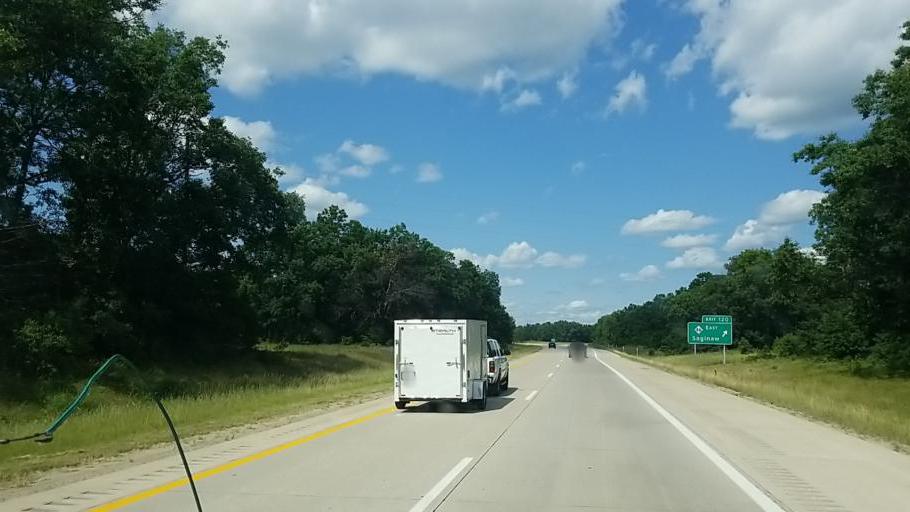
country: US
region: Michigan
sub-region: Montcalm County
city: Howard City
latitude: 43.4166
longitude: -85.5012
